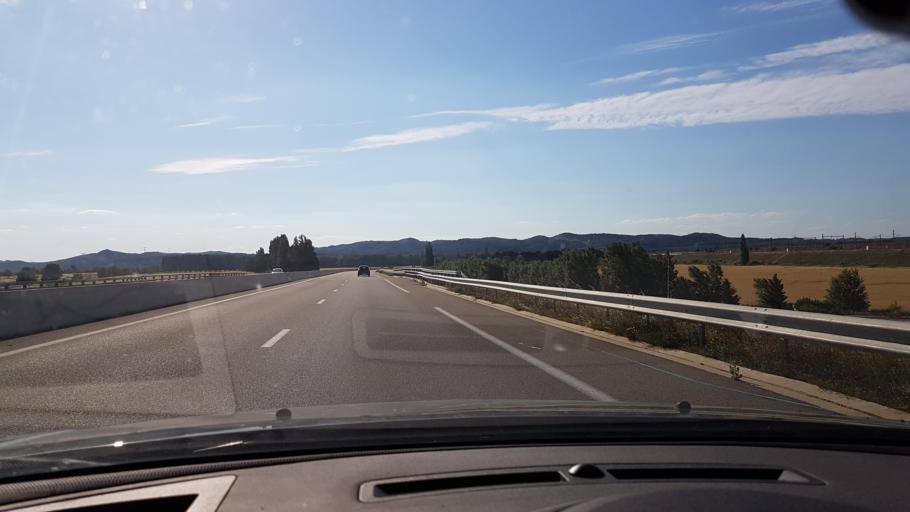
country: FR
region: Provence-Alpes-Cote d'Azur
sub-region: Departement des Bouches-du-Rhone
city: Rognonas
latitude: 43.9225
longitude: 4.7773
